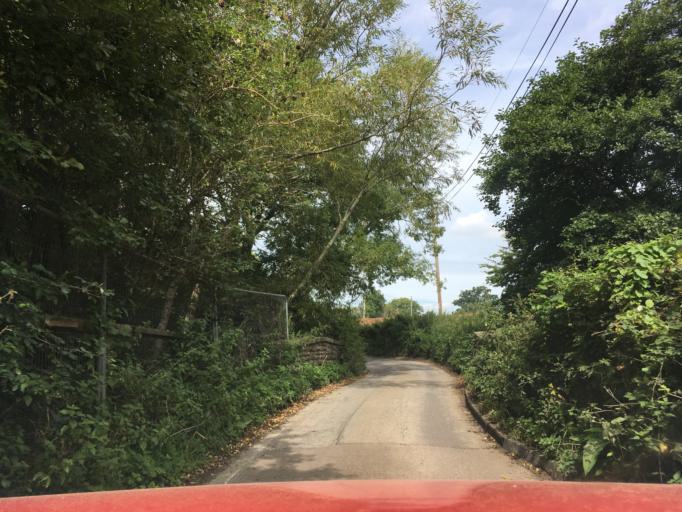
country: GB
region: England
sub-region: South Gloucestershire
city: Charfield
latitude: 51.6358
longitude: -2.4024
